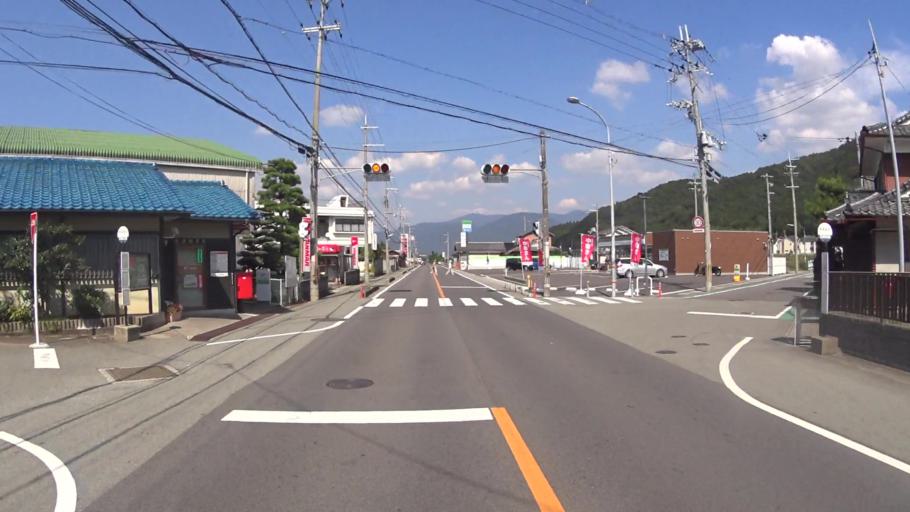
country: JP
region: Kyoto
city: Kameoka
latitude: 34.9991
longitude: 135.5522
